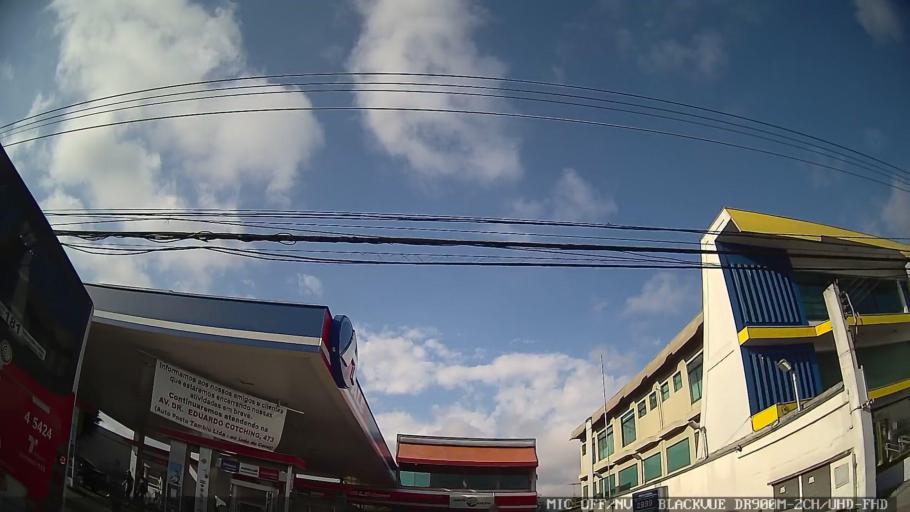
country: BR
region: Sao Paulo
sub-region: Sao Caetano Do Sul
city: Sao Caetano do Sul
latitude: -23.5646
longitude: -46.5468
